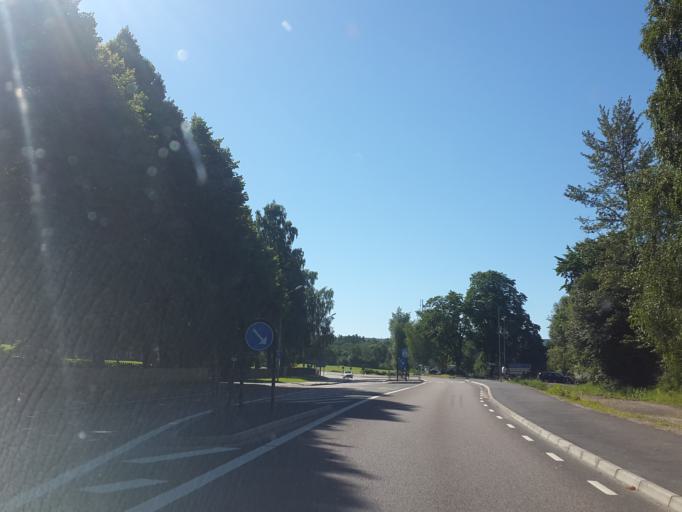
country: SE
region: Vaestra Goetaland
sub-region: Boras Kommun
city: Boras
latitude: 57.8191
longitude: 13.0080
